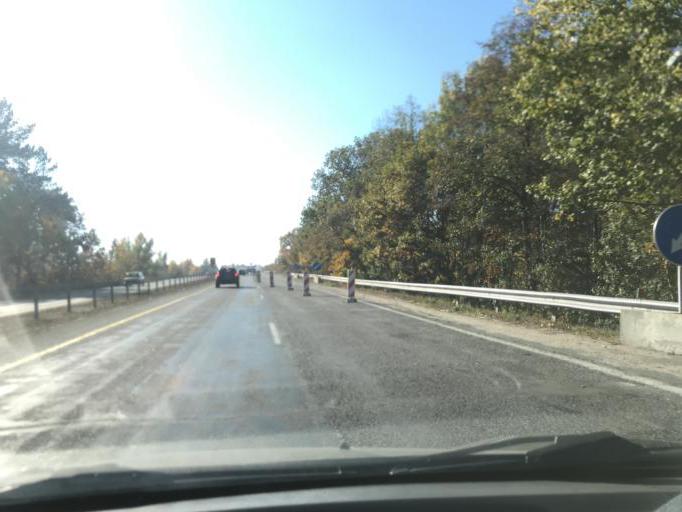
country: BY
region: Gomel
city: Horad Rechytsa
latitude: 52.3295
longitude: 30.5374
